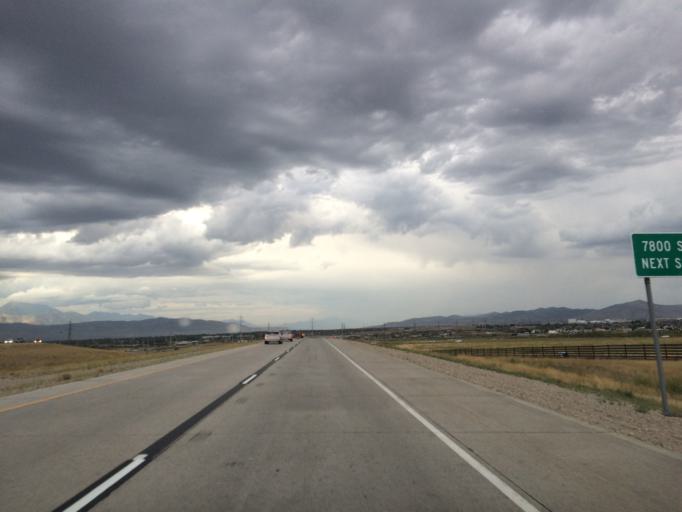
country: US
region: Utah
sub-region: Salt Lake County
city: Oquirrh
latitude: 40.6134
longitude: -112.0383
